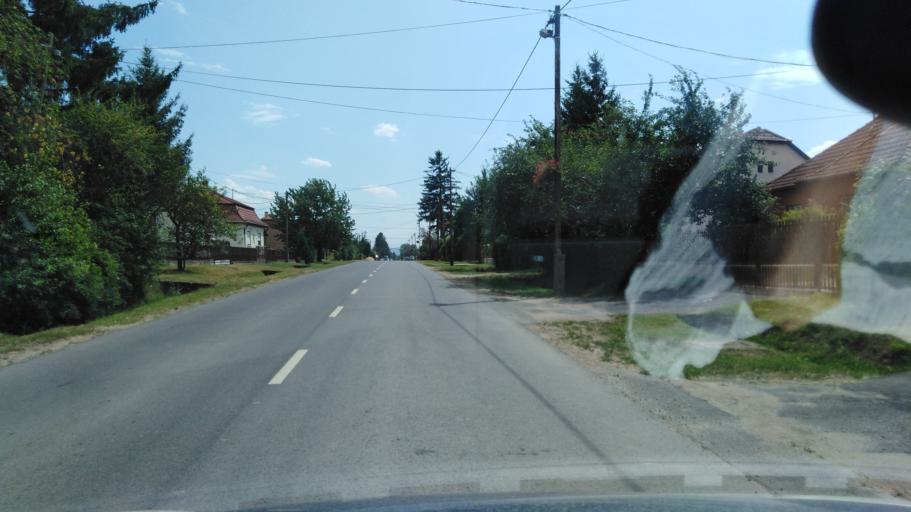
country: HU
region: Nograd
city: Szecseny
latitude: 48.1512
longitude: 19.5327
